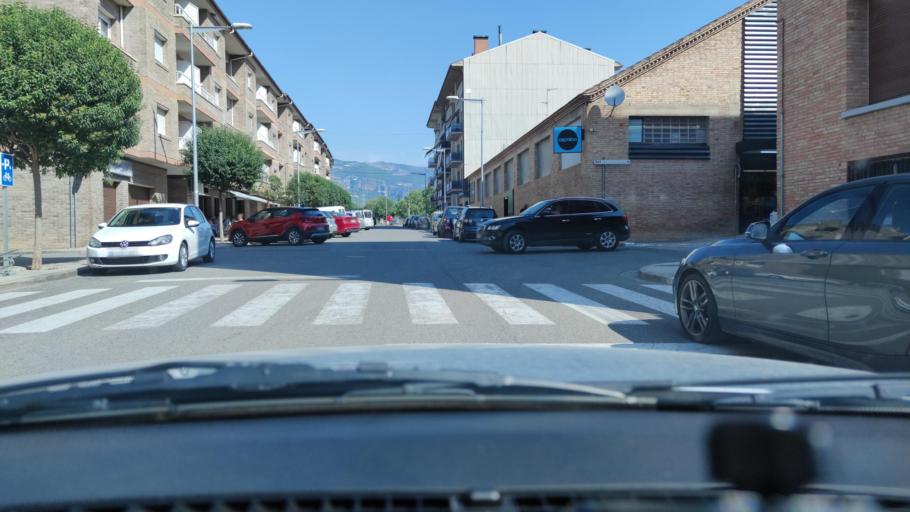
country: ES
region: Catalonia
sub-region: Provincia de Lleida
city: Senterada
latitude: 42.2502
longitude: 0.9650
